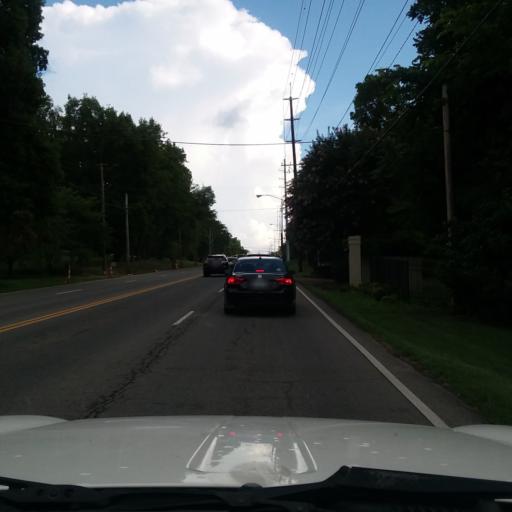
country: US
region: Tennessee
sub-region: Davidson County
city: Oak Hill
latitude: 36.0898
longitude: -86.7717
